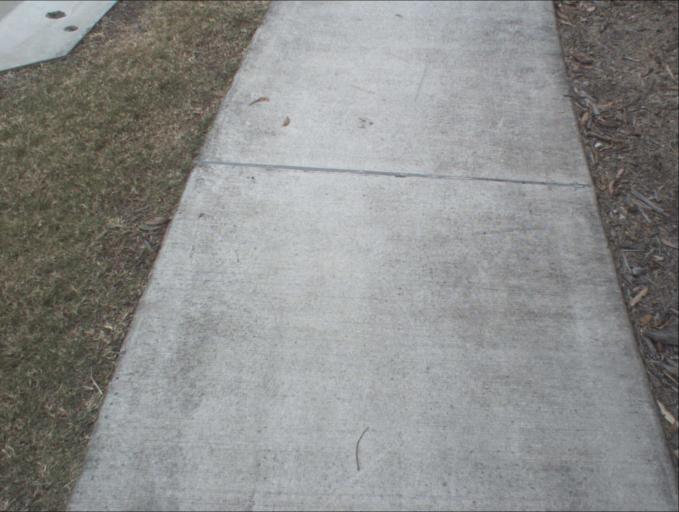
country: AU
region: Queensland
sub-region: Logan
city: Beenleigh
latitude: -27.6606
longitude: 153.2038
